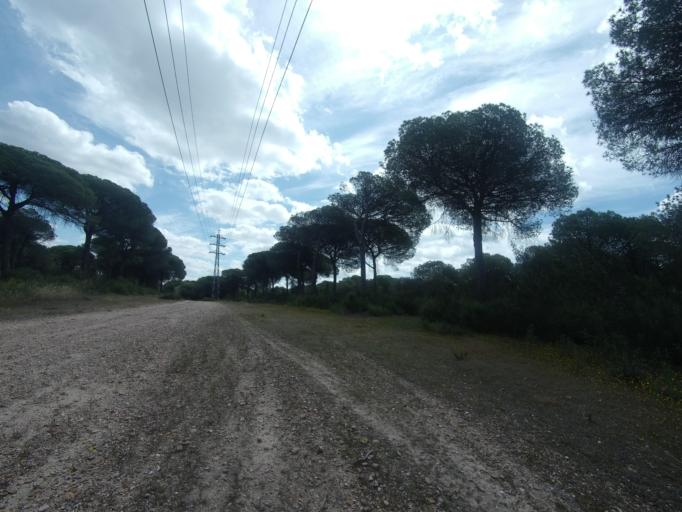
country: ES
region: Andalusia
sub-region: Provincia de Huelva
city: Aljaraque
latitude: 37.2245
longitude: -7.0664
